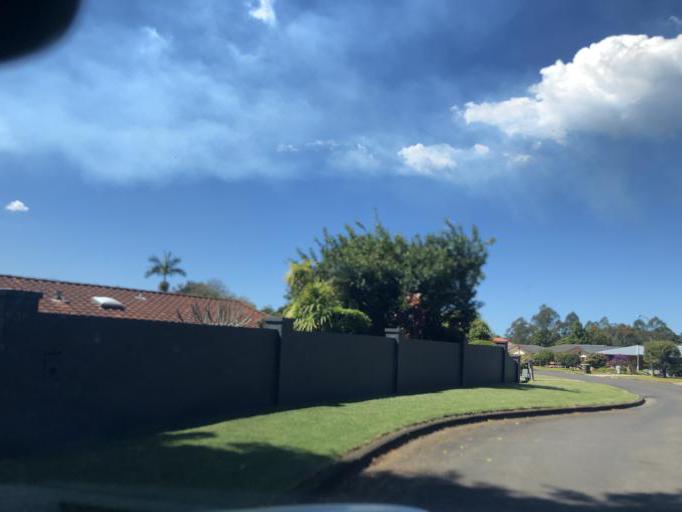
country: AU
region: New South Wales
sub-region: Bellingen
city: Bellingen
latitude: -30.4587
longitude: 152.9037
